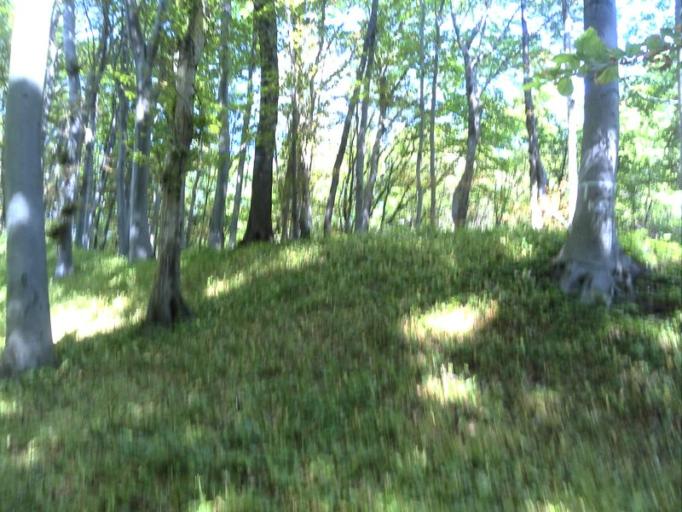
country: HU
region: Baranya
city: Pellerd
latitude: 46.0972
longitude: 18.1426
